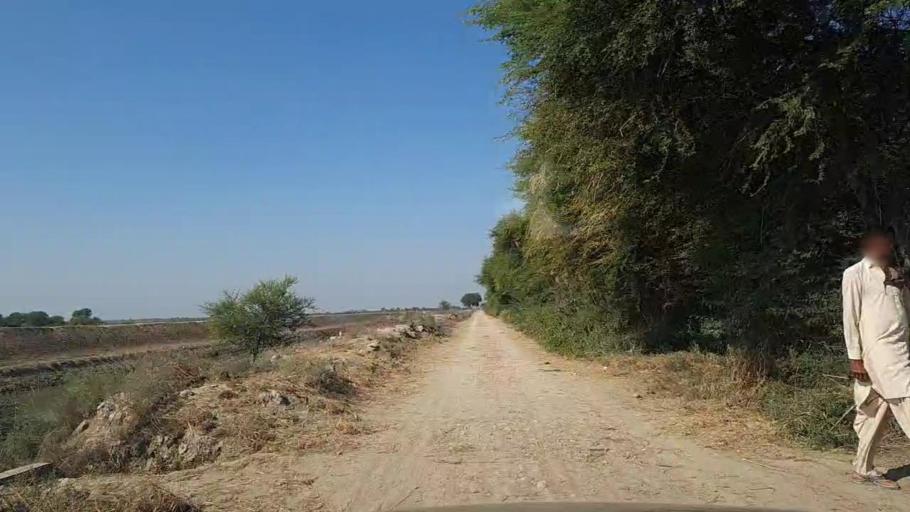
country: PK
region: Sindh
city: Mirpur Batoro
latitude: 24.7194
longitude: 68.2353
